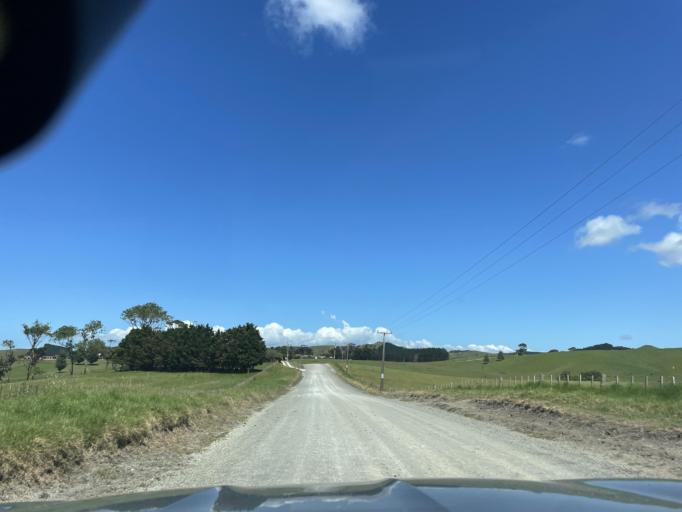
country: NZ
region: Auckland
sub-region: Auckland
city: Wellsford
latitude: -36.2868
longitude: 174.3439
